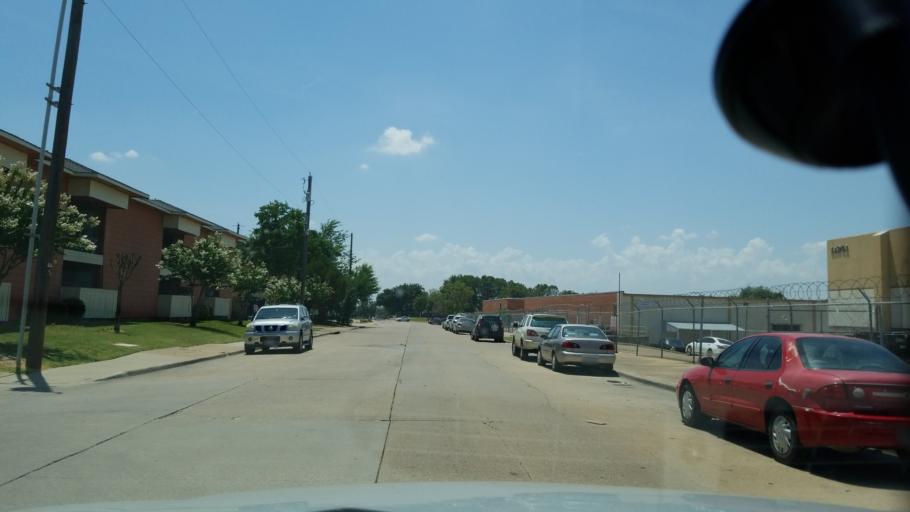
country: US
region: Texas
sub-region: Dallas County
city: Farmers Branch
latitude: 32.8927
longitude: -96.8831
